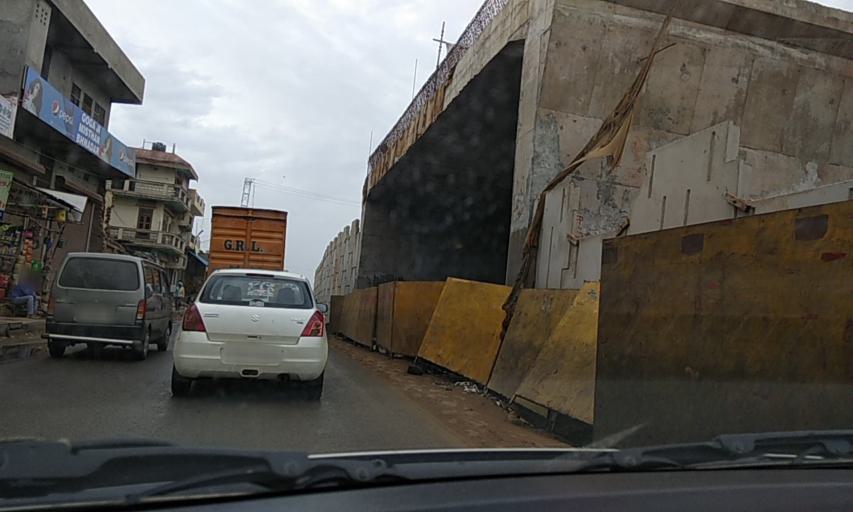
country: IN
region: Haryana
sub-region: Palwal
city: Palwal
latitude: 28.0607
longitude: 77.3473
